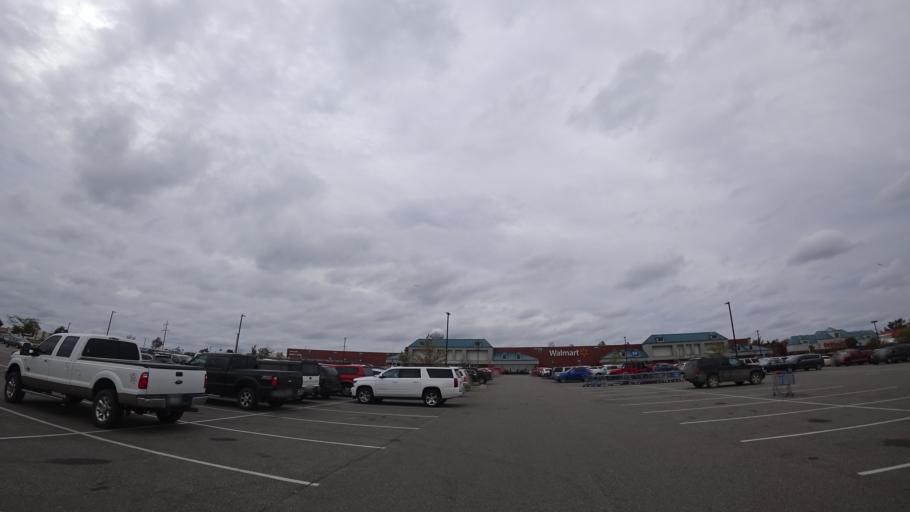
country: US
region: Michigan
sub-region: Emmet County
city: Petoskey
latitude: 45.3502
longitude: -84.9719
